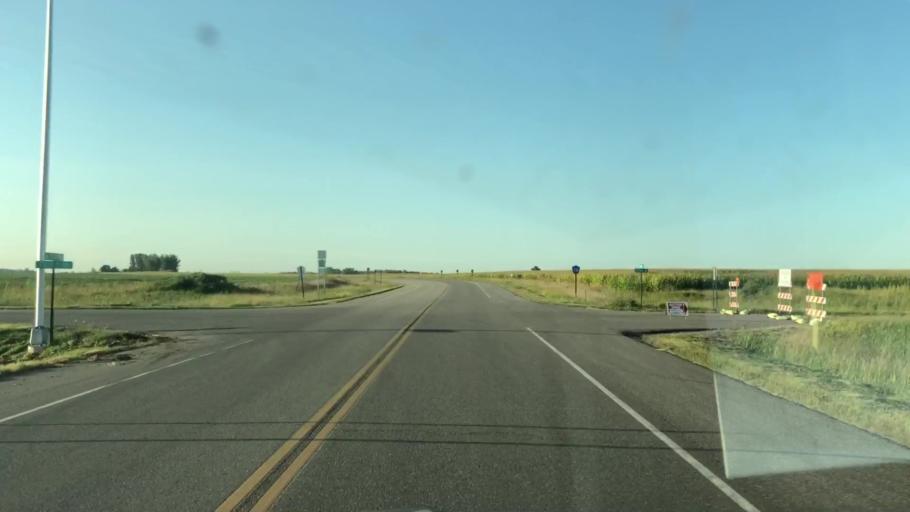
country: US
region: Minnesota
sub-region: Nobles County
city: Worthington
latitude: 43.6024
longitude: -95.6366
